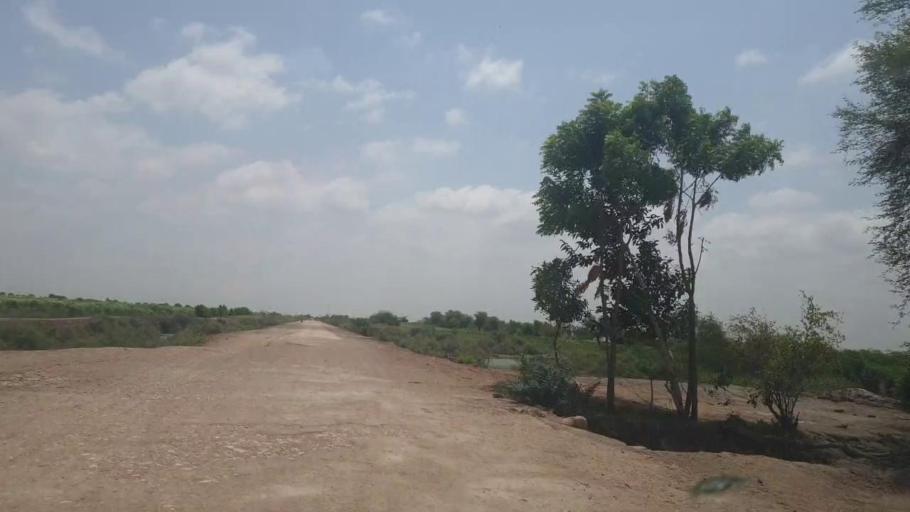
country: PK
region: Sindh
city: Tando Mittha Khan
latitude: 25.9182
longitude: 69.1985
